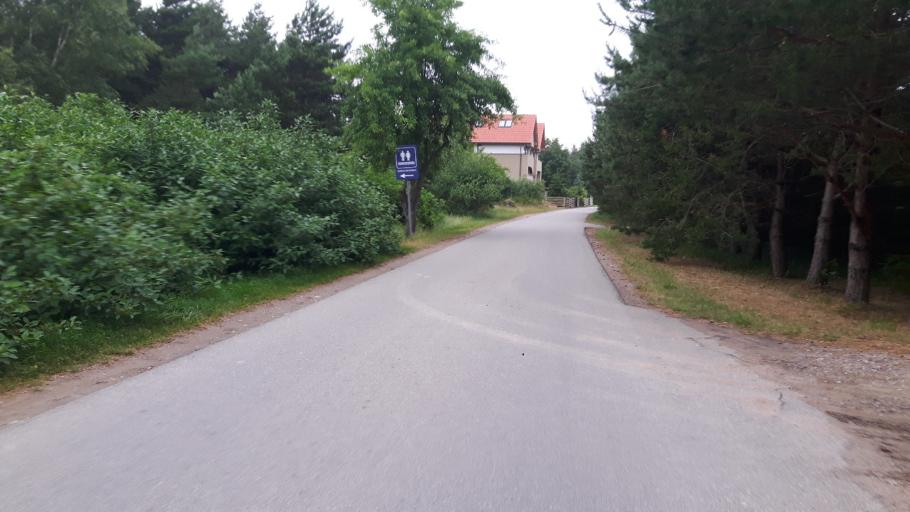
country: LT
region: Klaipedos apskritis
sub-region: Palanga
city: Sventoji
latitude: 56.0117
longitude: 21.0756
